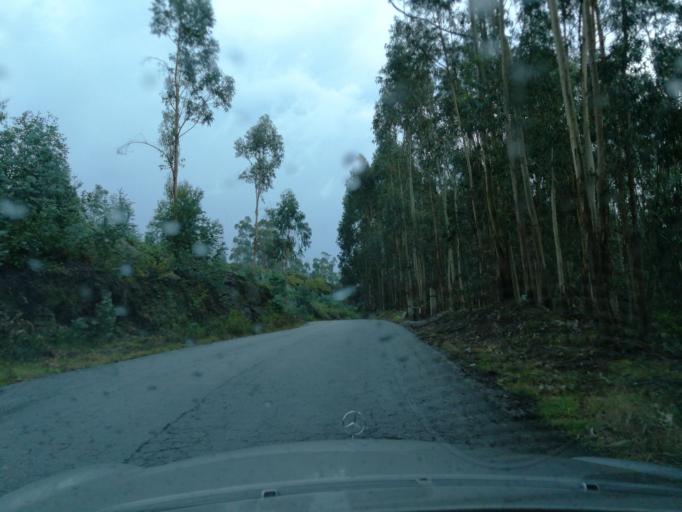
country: PT
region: Braga
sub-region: Braga
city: Oliveira
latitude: 41.4663
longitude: -8.4375
